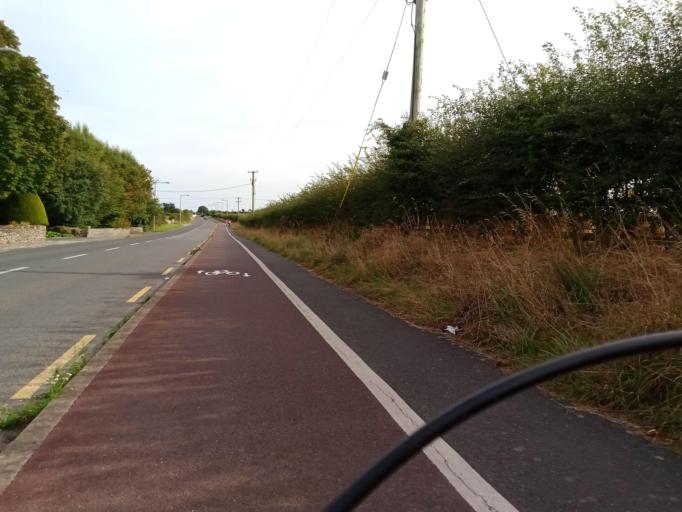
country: IE
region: Munster
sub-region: Waterford
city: Dungarvan
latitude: 52.0979
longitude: -7.5610
